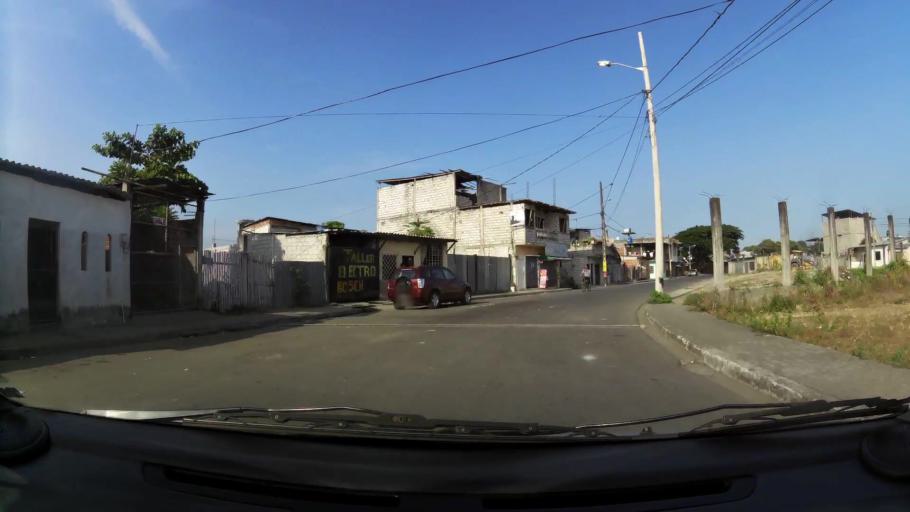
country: EC
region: Guayas
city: Eloy Alfaro
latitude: -2.1855
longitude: -79.8395
